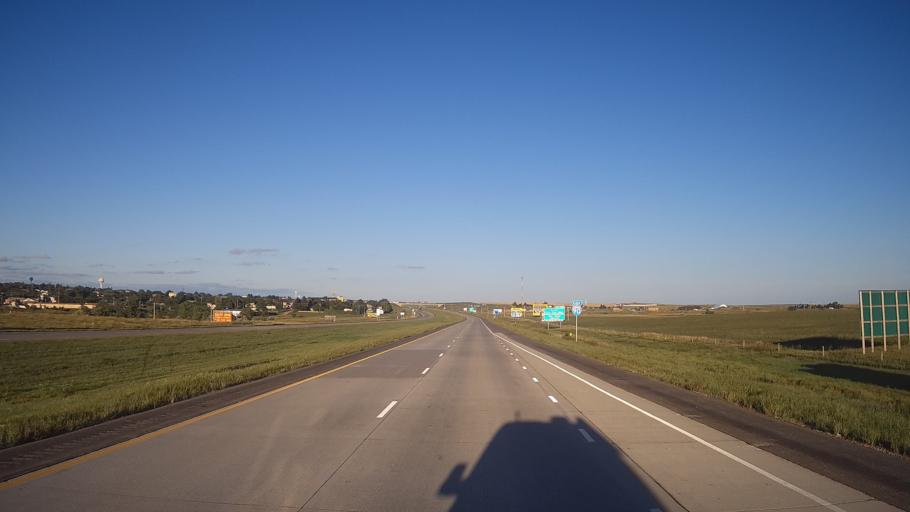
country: US
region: South Dakota
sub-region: Jones County
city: Murdo
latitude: 43.8838
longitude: -100.7245
